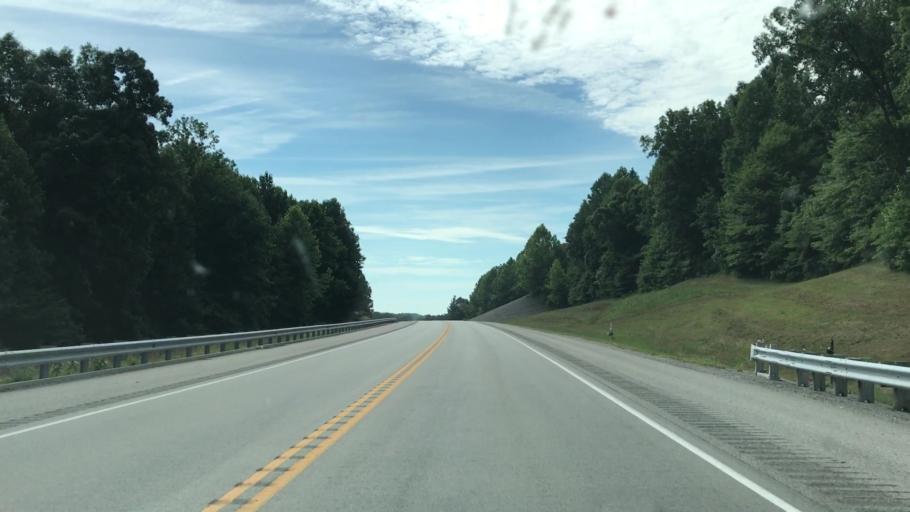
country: US
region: Kentucky
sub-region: Edmonson County
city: Brownsville
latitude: 37.1795
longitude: -86.2436
